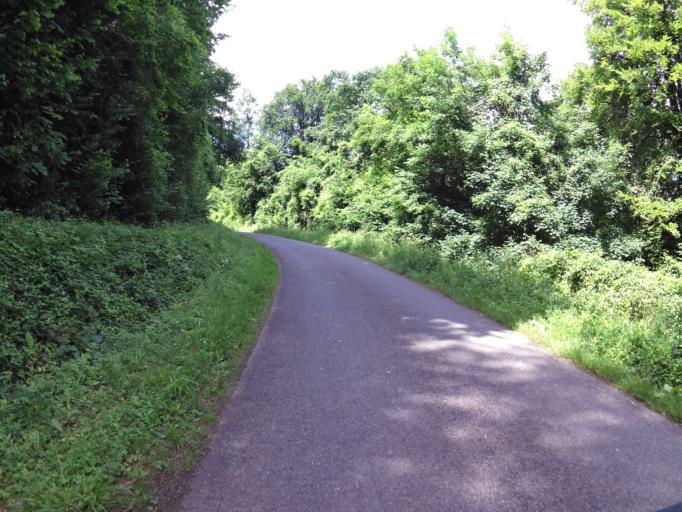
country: FR
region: Lorraine
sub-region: Departement de la Meuse
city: Stenay
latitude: 49.5399
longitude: 5.1355
